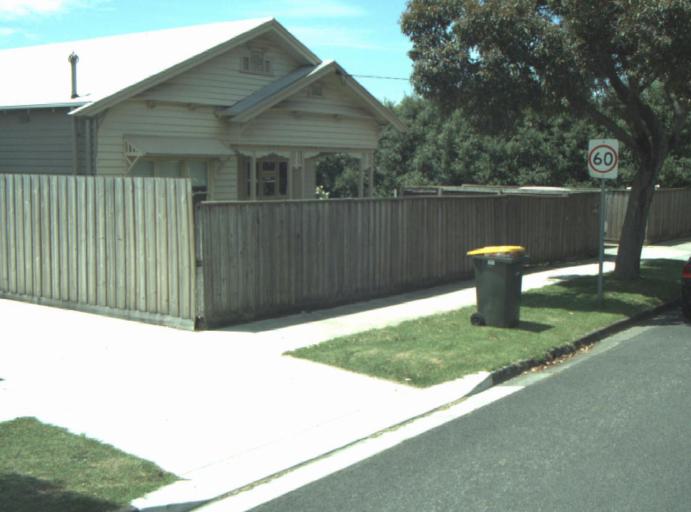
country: AU
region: Victoria
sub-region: Greater Geelong
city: Hamlyn Heights
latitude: -38.1406
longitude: 144.3274
